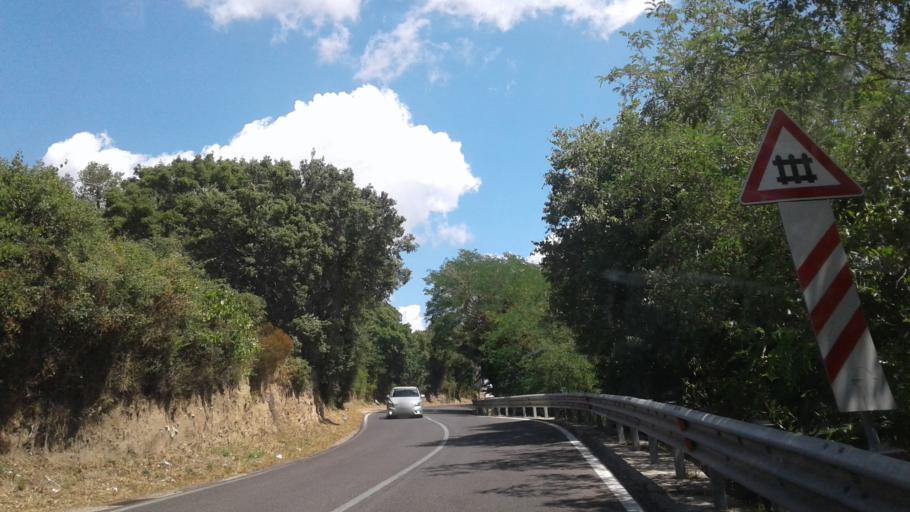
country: IT
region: Sardinia
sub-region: Provincia di Olbia-Tempio
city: Luras
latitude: 40.9195
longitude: 9.1748
